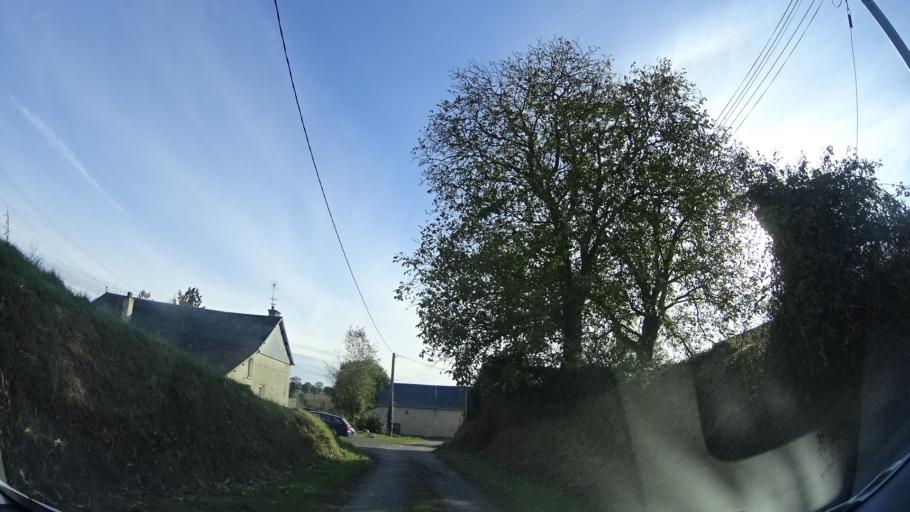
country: FR
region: Brittany
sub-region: Departement d'Ille-et-Vilaine
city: Geveze
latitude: 48.2193
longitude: -1.8082
